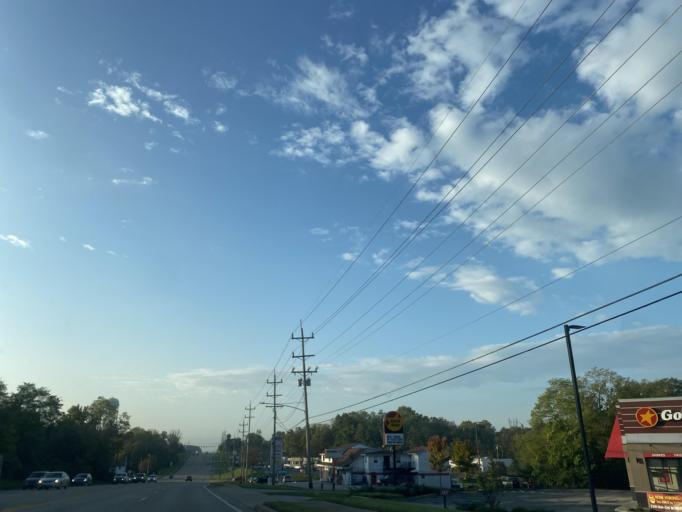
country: US
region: Kentucky
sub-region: Campbell County
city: Alexandria
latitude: 38.9635
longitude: -84.3929
